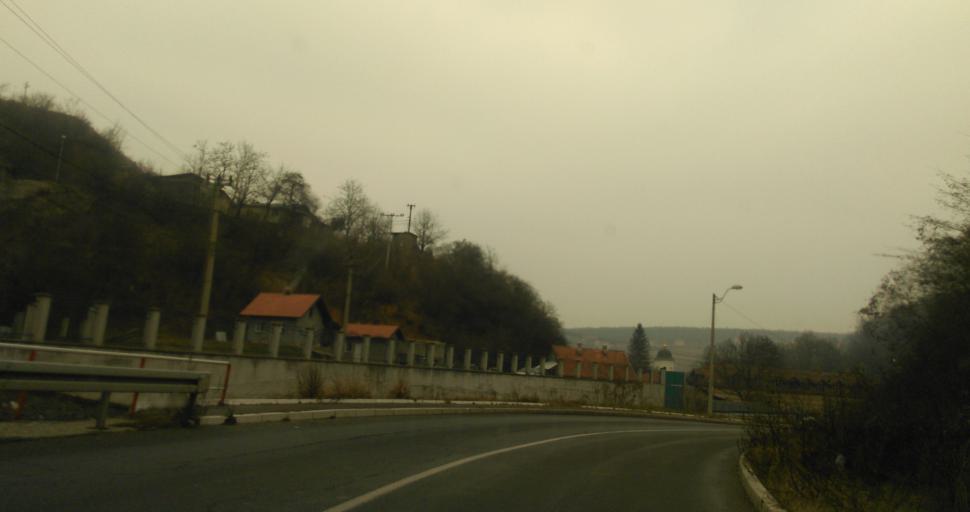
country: RS
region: Central Serbia
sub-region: Belgrade
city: Rakovica
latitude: 44.7290
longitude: 20.4466
